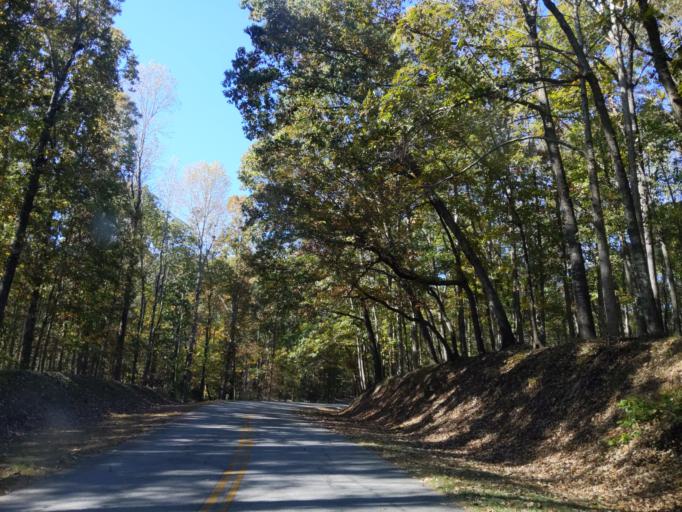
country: US
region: Georgia
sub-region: Franklin County
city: Gumlog
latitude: 34.4950
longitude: -83.0644
